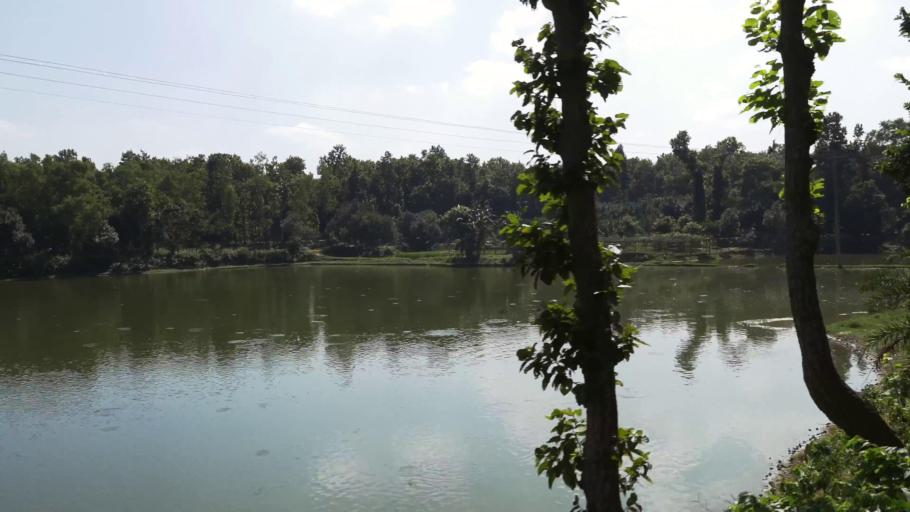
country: BD
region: Dhaka
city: Gafargaon
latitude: 24.2376
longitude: 90.4912
